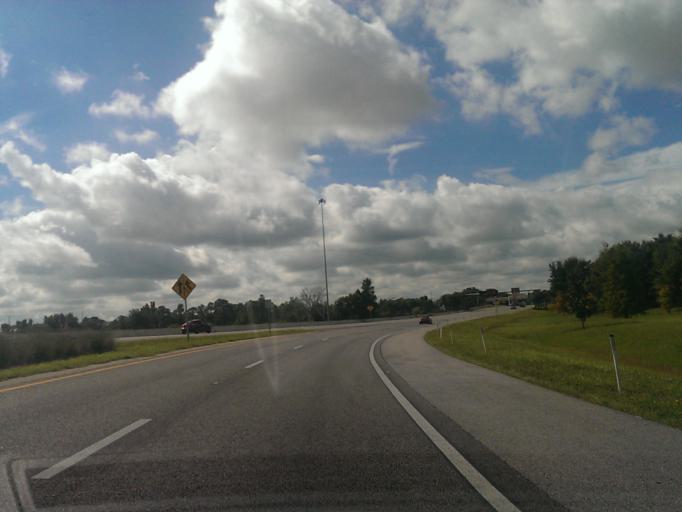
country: US
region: Florida
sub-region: Orange County
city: Belle Isle
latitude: 28.4469
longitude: -81.3093
